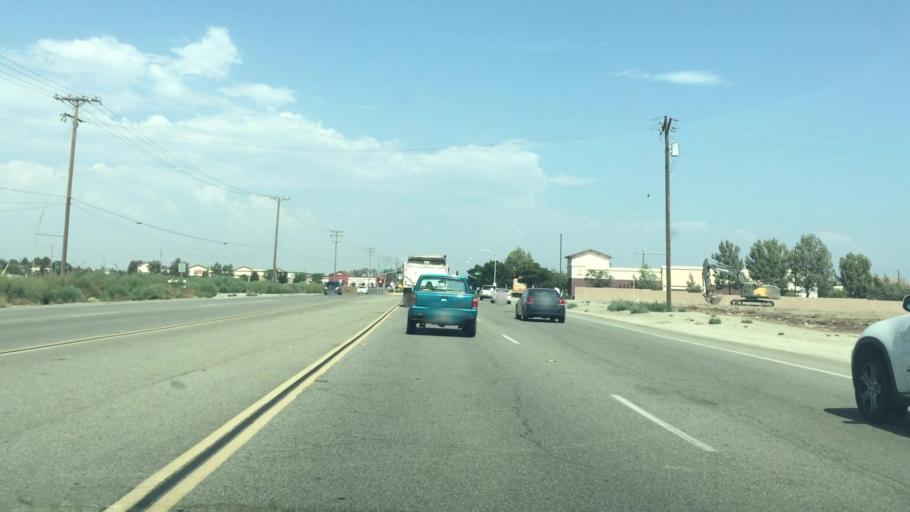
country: US
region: California
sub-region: Riverside County
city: Norco
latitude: 33.9753
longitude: -117.5640
